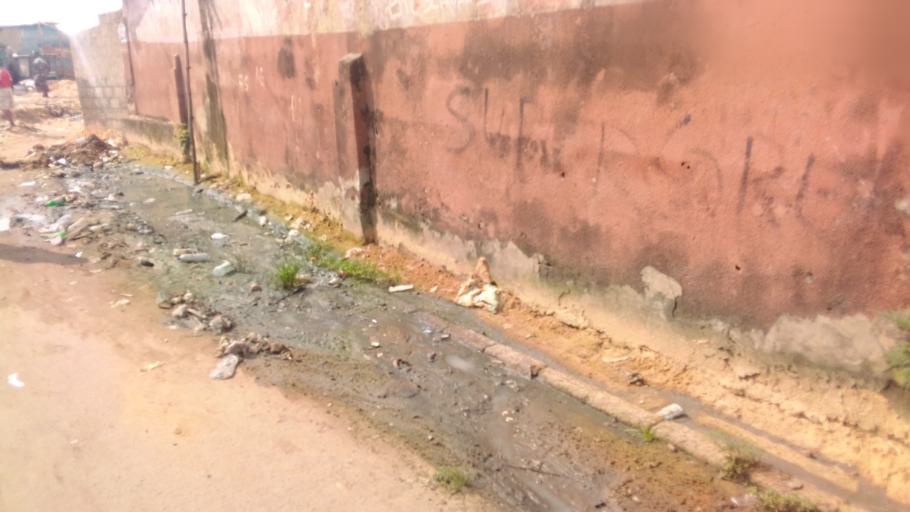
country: CD
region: Kinshasa
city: Masina
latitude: -4.3965
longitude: 15.3443
